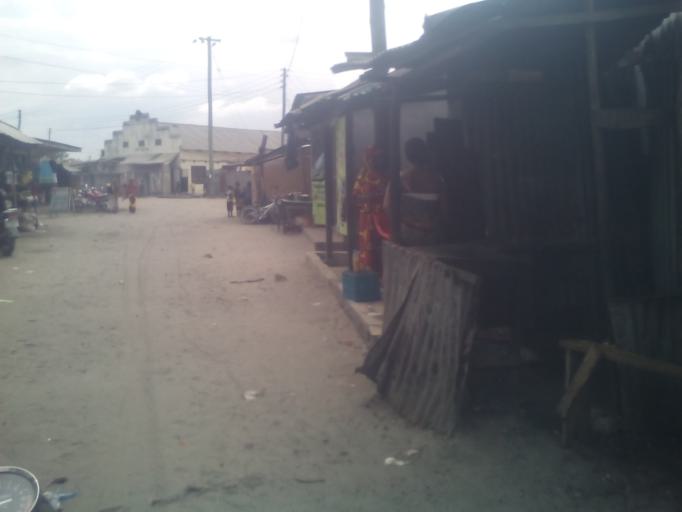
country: TZ
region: Dar es Salaam
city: Dar es Salaam
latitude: -6.8605
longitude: 39.2423
